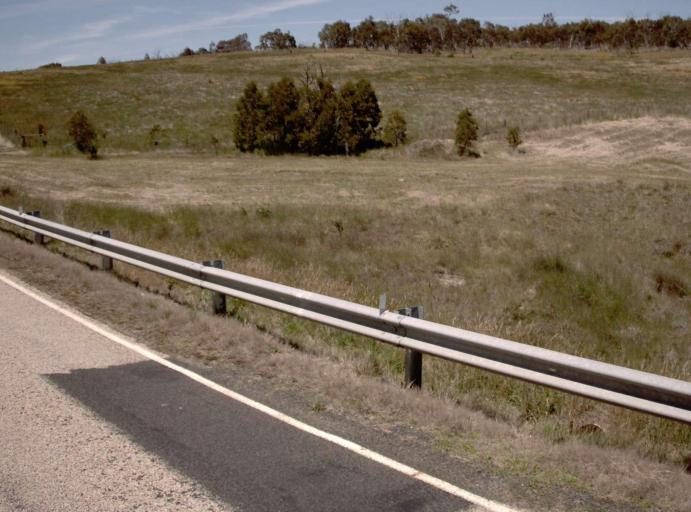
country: AU
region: Victoria
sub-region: Alpine
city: Mount Beauty
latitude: -37.1187
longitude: 147.6207
